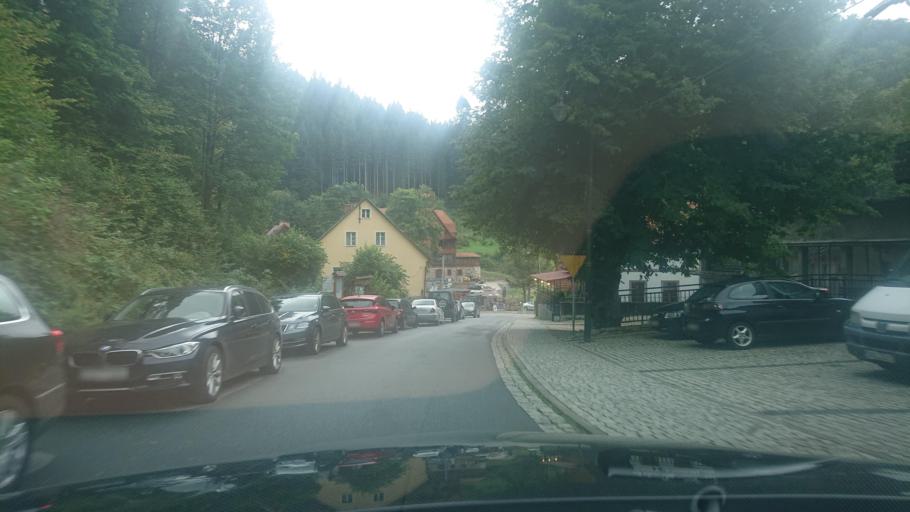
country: PL
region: Lower Silesian Voivodeship
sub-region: Powiat klodzki
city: Stronie Slaskie
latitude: 50.2293
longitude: 16.7655
